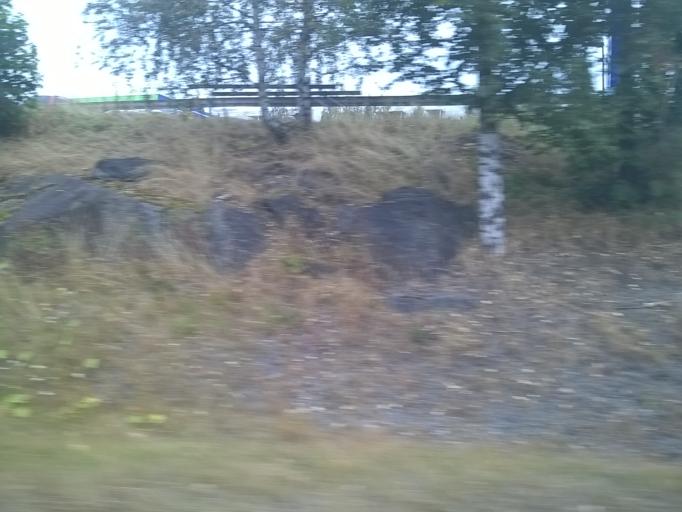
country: FI
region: Pirkanmaa
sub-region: Tampere
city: Tampere
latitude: 61.4546
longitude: 23.8483
